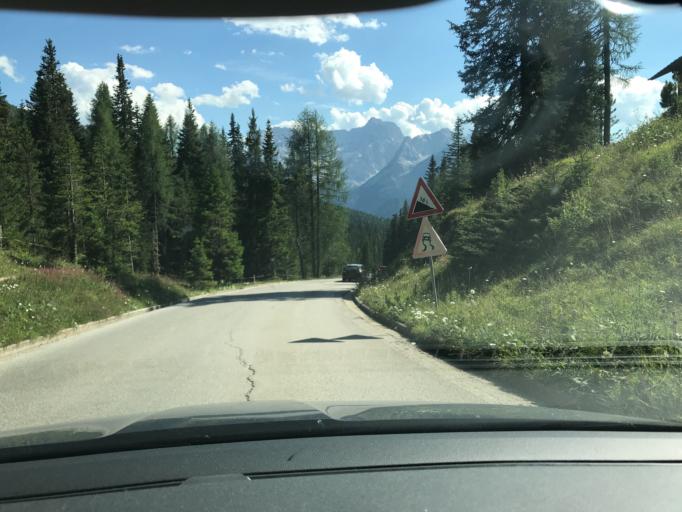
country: IT
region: Veneto
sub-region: Provincia di Belluno
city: Cortina d'Ampezzo
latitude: 46.5932
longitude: 12.2639
